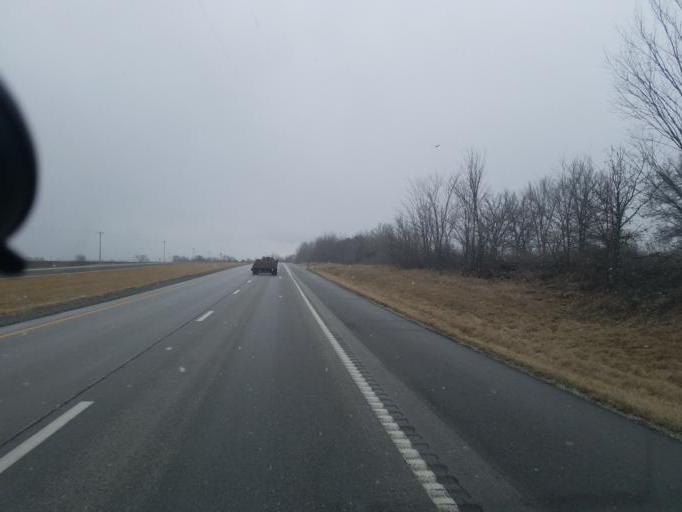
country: US
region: Missouri
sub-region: Macon County
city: Macon
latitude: 39.8727
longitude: -92.4774
